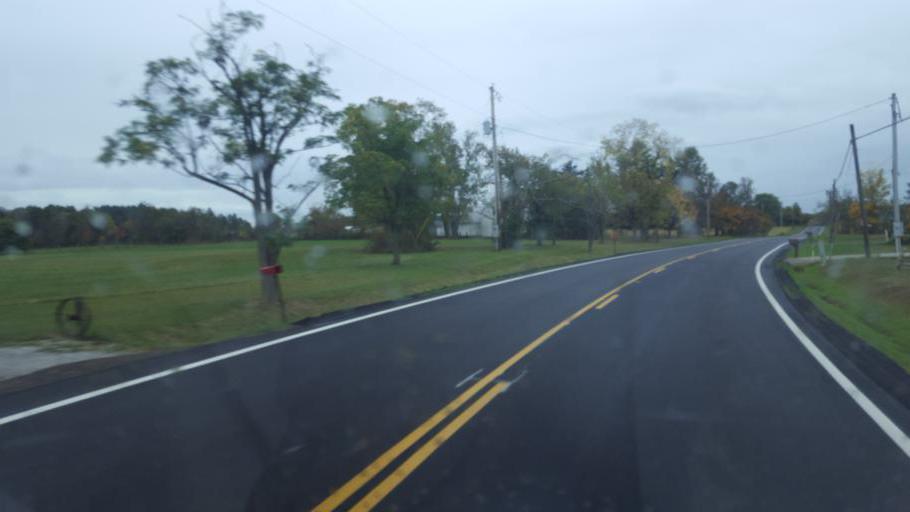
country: US
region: Ohio
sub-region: Huron County
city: New London
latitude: 41.0136
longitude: -82.3848
